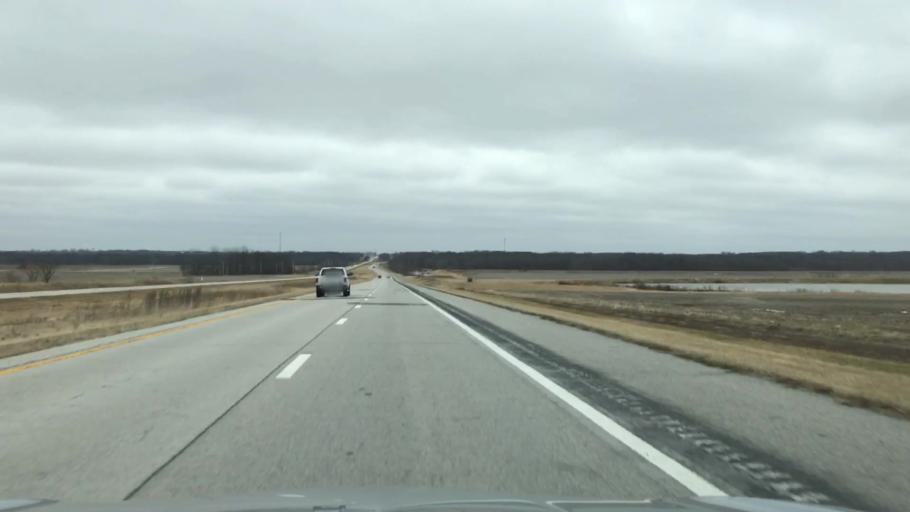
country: US
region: Missouri
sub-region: Linn County
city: Linneus
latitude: 39.7781
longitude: -93.3409
